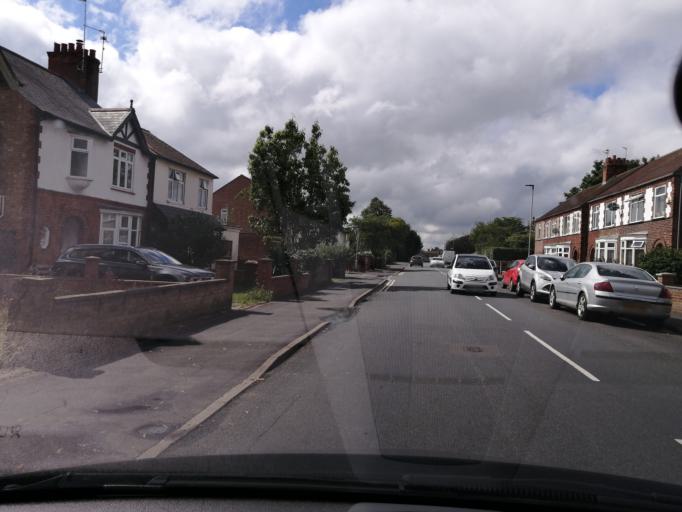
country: GB
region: England
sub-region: Peterborough
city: Peterborough
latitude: 52.5599
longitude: -0.2506
